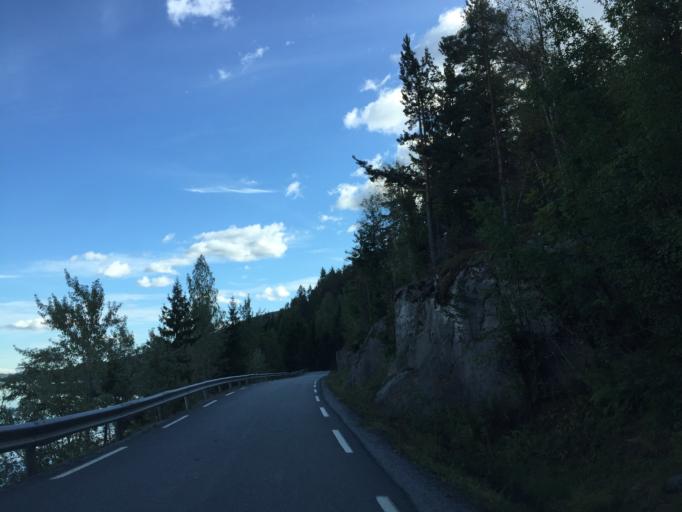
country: NO
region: Buskerud
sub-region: Ovre Eiker
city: Hokksund
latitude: 59.6532
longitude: 9.9145
